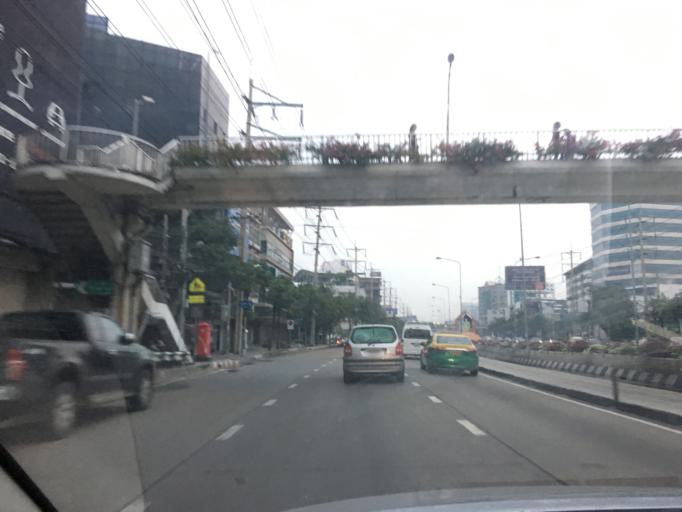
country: TH
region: Bangkok
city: Bang Kho Laem
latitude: 13.6909
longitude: 100.5028
